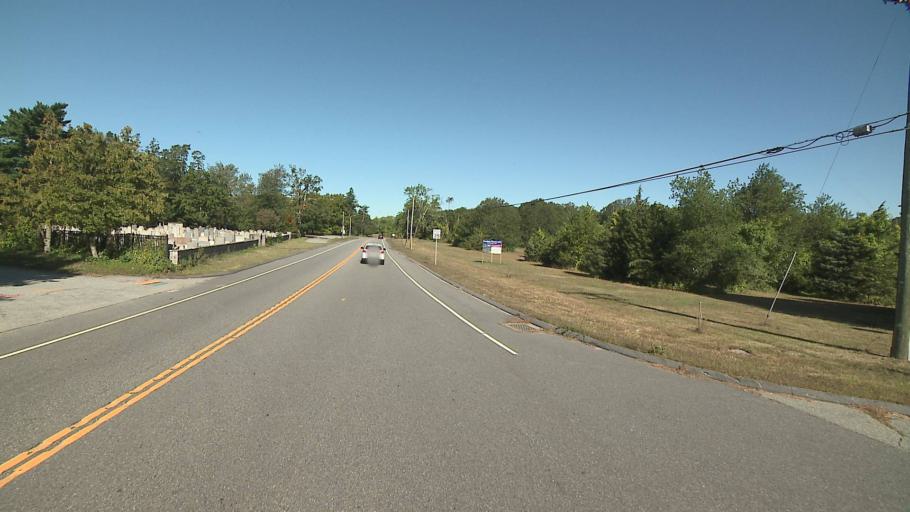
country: US
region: Connecticut
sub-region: New London County
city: Norwich
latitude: 41.4876
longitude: -72.0678
